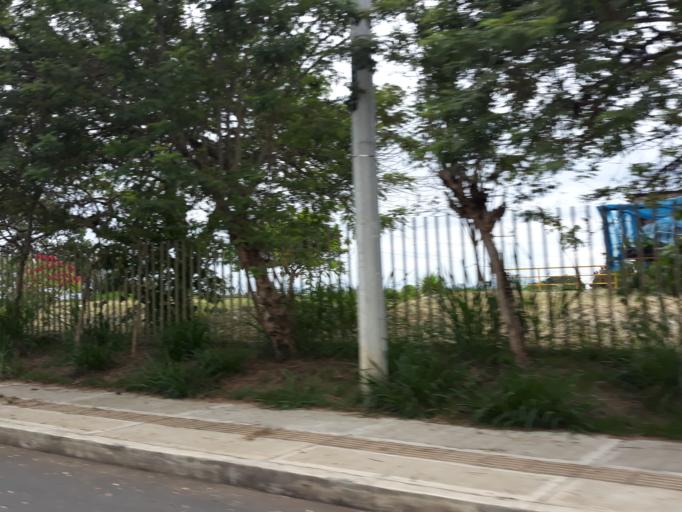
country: CO
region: Valle del Cauca
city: Jamundi
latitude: 3.3465
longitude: -76.5518
